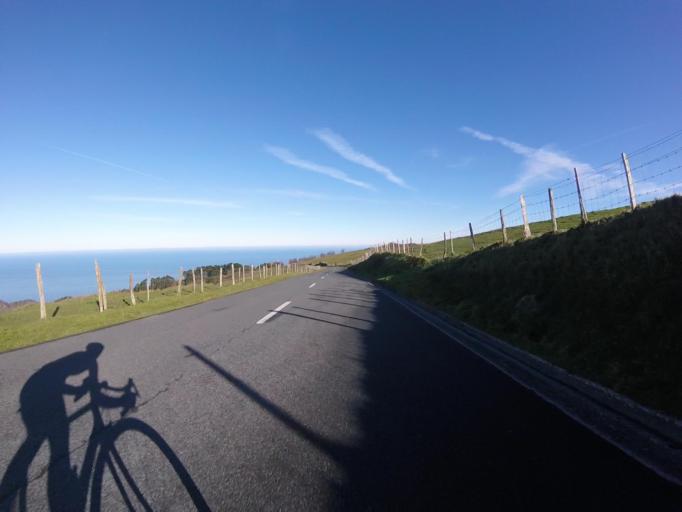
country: ES
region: Basque Country
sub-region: Provincia de Guipuzcoa
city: Fuenterrabia
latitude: 43.3538
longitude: -1.8424
